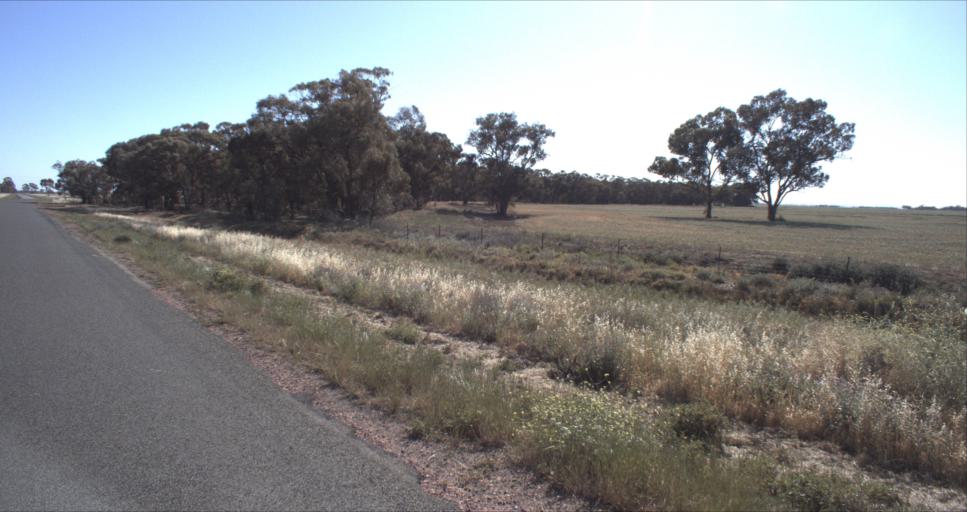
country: AU
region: New South Wales
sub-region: Leeton
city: Leeton
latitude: -34.5645
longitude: 146.2647
